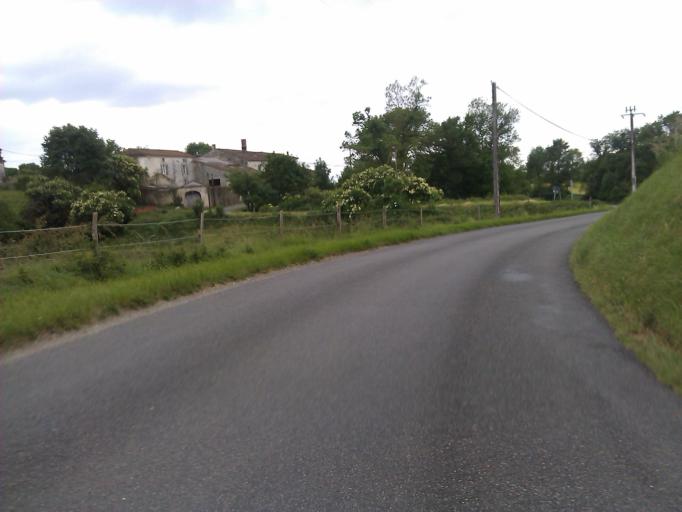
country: FR
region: Poitou-Charentes
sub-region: Departement de la Charente
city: Sireuil
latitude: 45.6415
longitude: 0.0214
